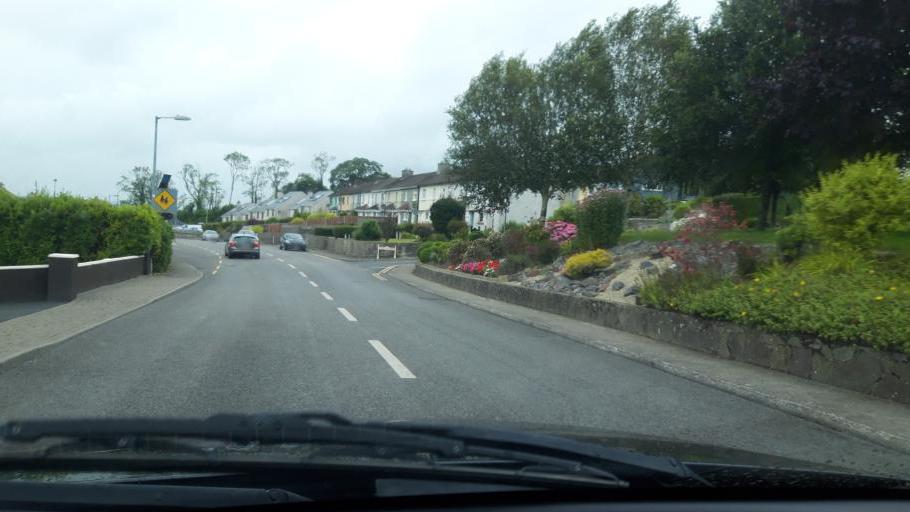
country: IE
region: Munster
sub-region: County Cork
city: Youghal
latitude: 52.1466
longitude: -7.8392
